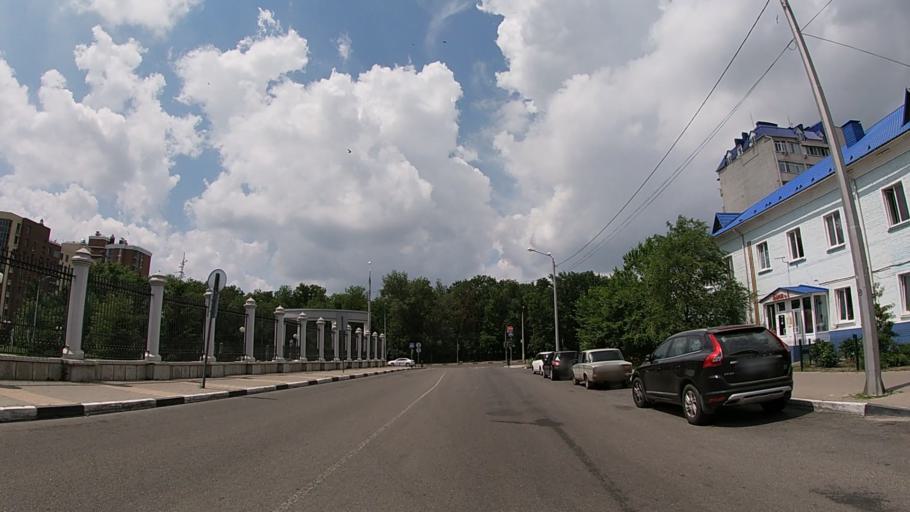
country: RU
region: Belgorod
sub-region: Belgorodskiy Rayon
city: Belgorod
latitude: 50.6069
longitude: 36.5924
